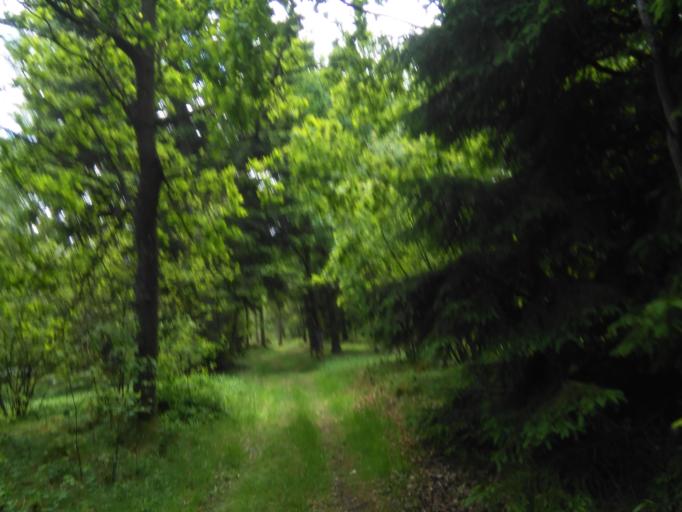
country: DK
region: Capital Region
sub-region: Bornholm Kommune
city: Nexo
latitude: 55.0944
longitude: 15.1035
